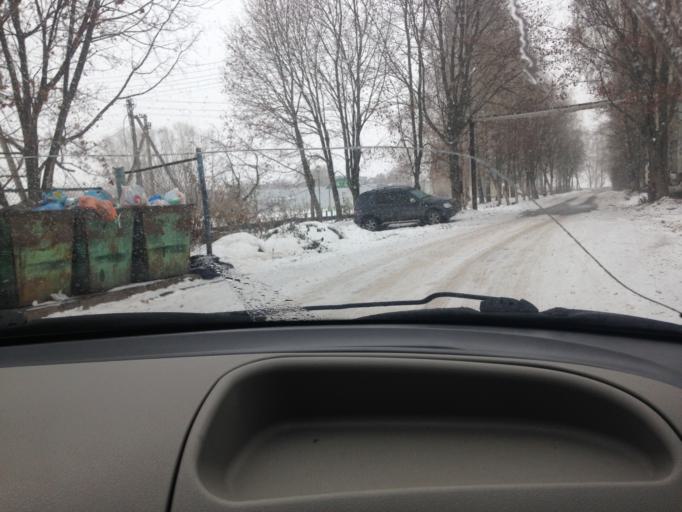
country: RU
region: Tula
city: Shchekino
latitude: 53.8516
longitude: 37.4819
